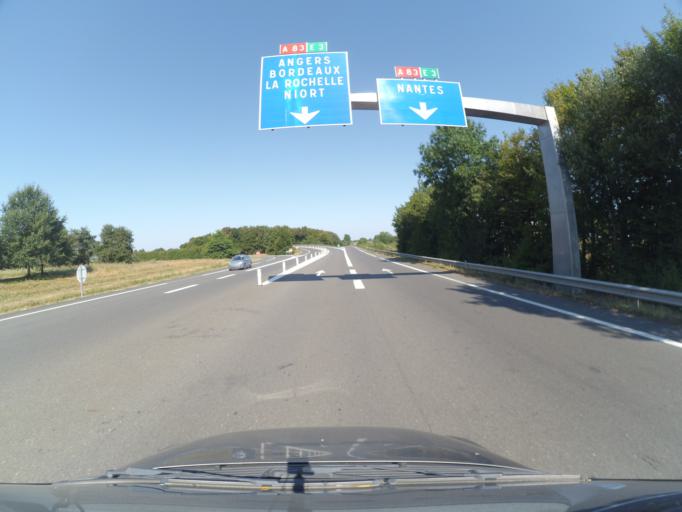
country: FR
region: Pays de la Loire
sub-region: Departement de la Vendee
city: Bouffere
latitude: 46.9603
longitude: -1.3548
